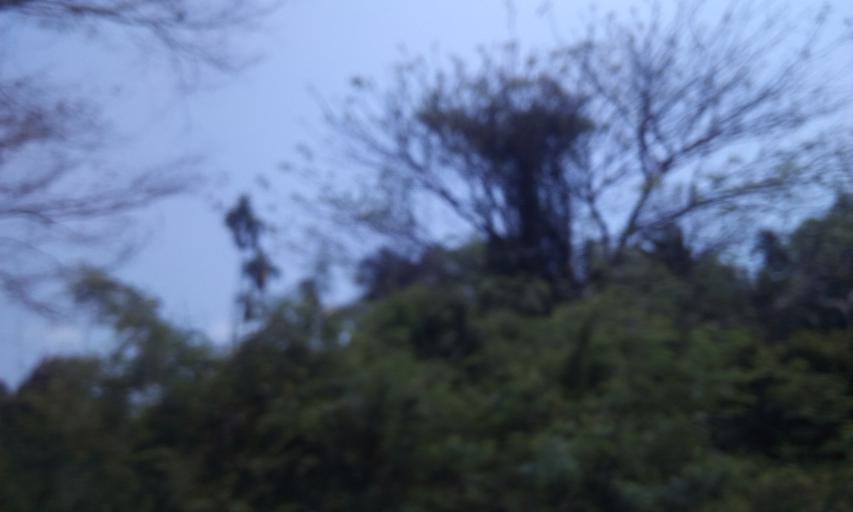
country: TH
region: Chachoengsao
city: Bang Nam Priao
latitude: 13.8766
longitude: 100.9677
